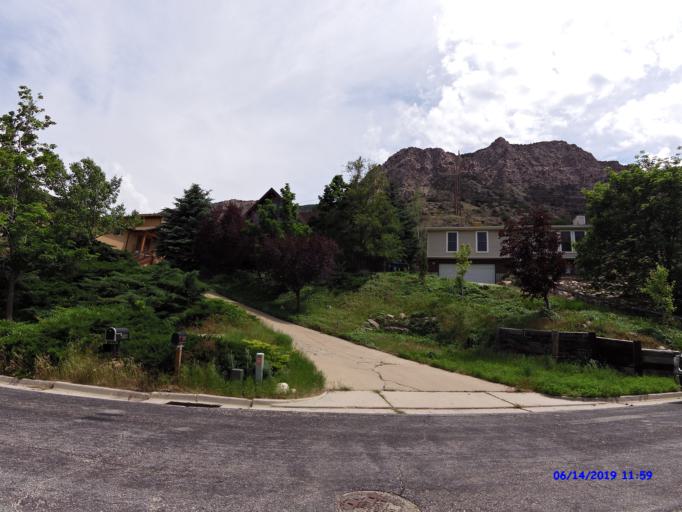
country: US
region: Utah
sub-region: Weber County
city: North Ogden
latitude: 41.2634
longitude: -111.9456
